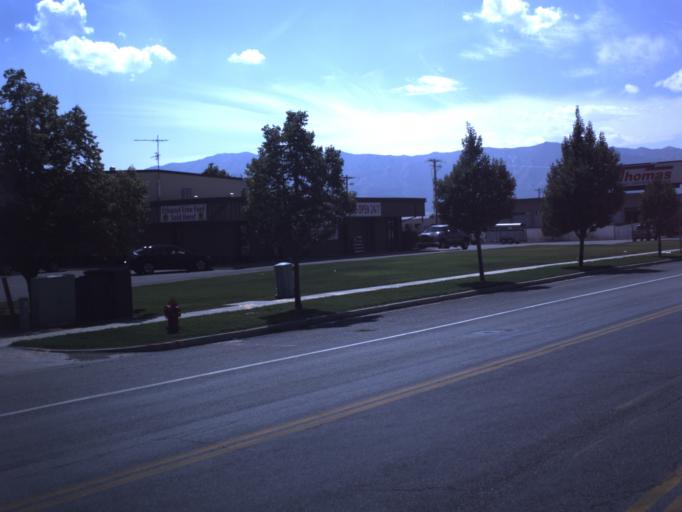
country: US
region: Utah
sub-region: Cache County
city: Logan
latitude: 41.7357
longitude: -111.8619
